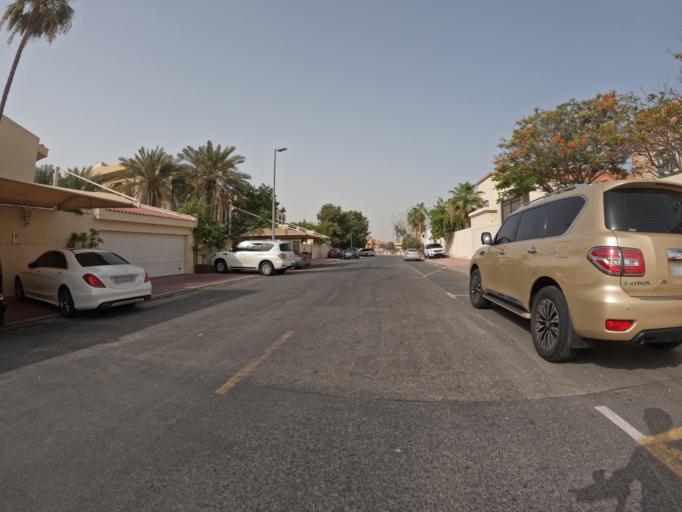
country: AE
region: Dubai
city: Dubai
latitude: 25.1976
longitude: 55.2387
